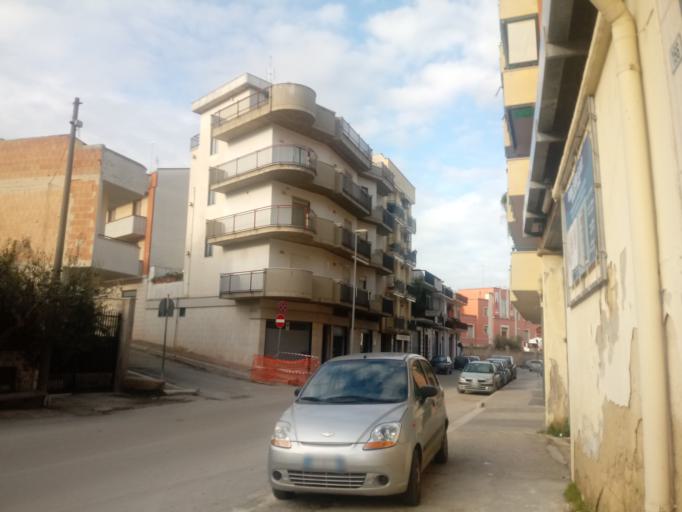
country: IT
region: Apulia
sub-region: Provincia di Barletta - Andria - Trani
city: Andria
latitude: 41.2170
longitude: 16.2959
